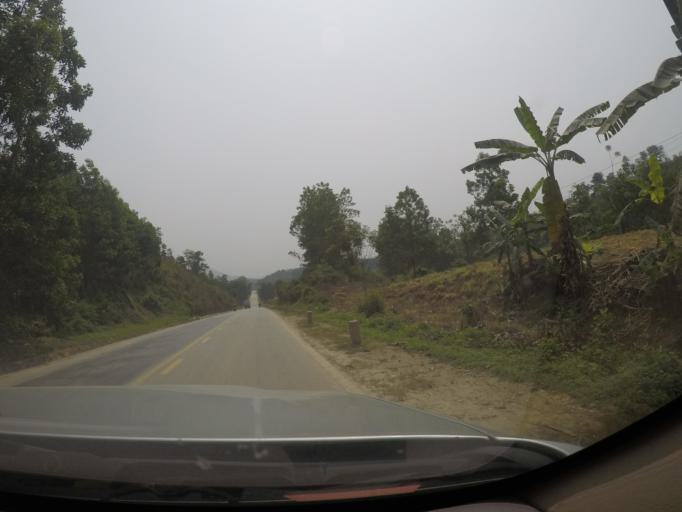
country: VN
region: Thanh Hoa
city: Thi Tran Thuong Xuan
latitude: 19.8255
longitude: 105.3898
